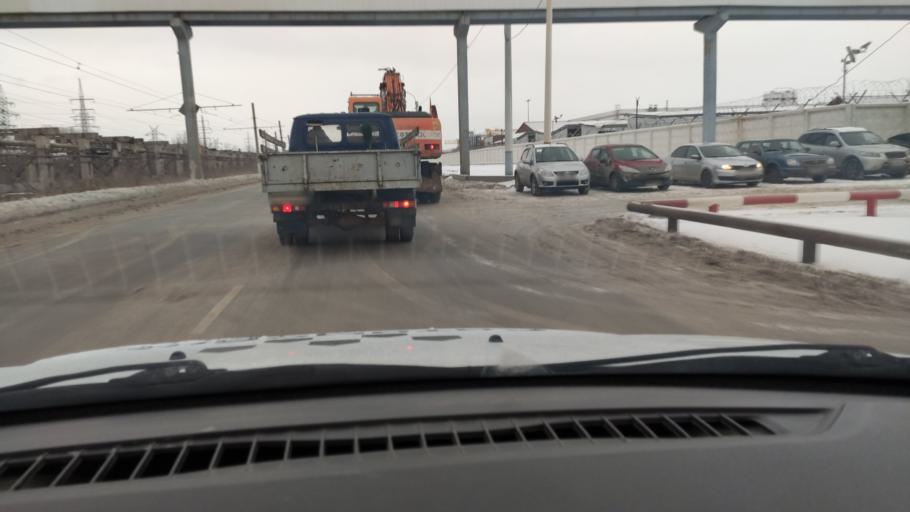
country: RU
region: Perm
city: Gamovo
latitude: 57.9213
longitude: 56.1436
